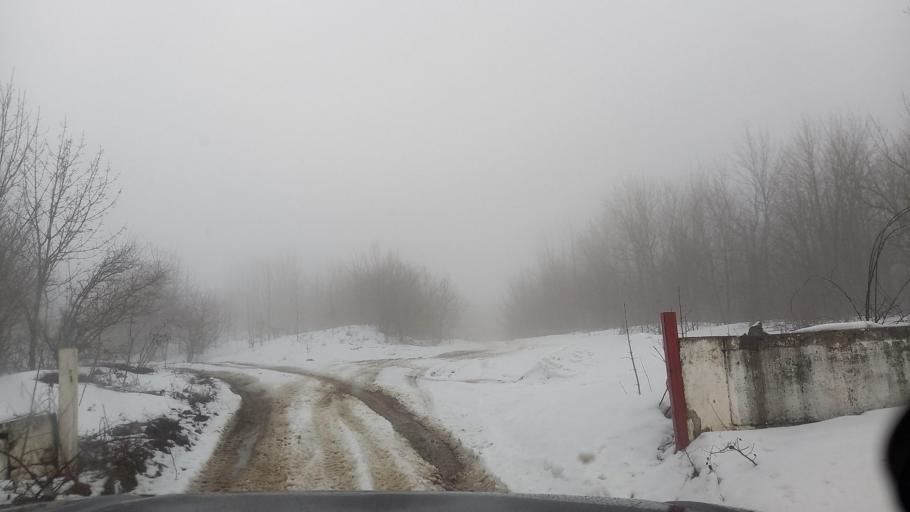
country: RU
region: Krasnodarskiy
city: Divnomorskoye
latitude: 44.6084
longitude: 38.2563
